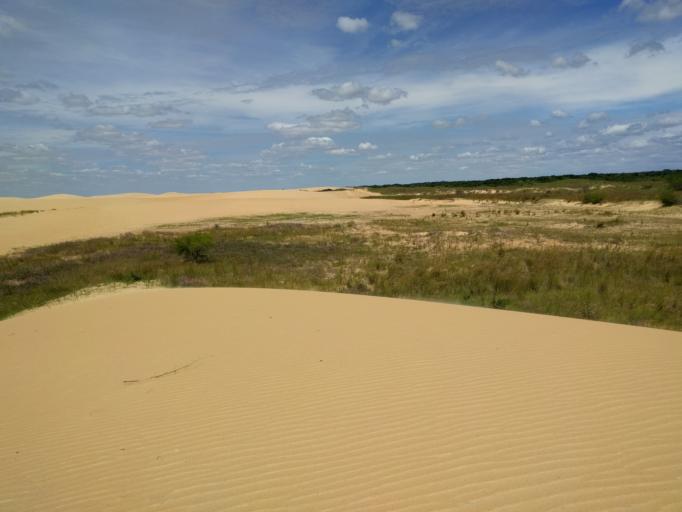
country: BO
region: Santa Cruz
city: Santa Cruz de la Sierra
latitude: -17.9536
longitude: -63.1552
